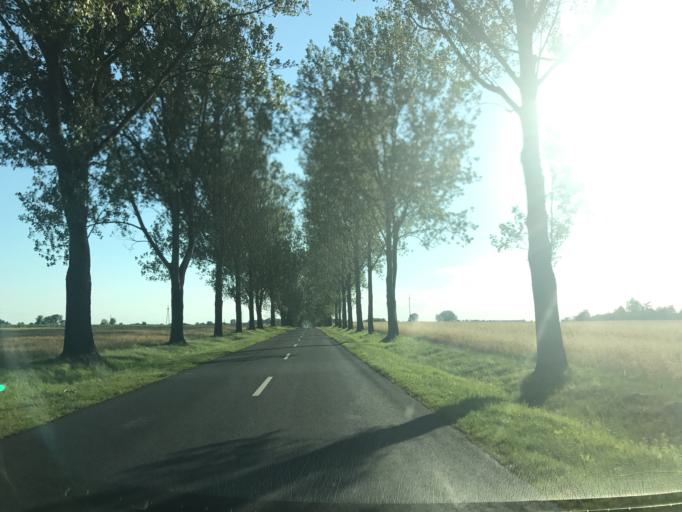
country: PL
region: Greater Poland Voivodeship
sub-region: Powiat koninski
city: Rychwal
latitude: 52.0755
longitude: 18.1888
